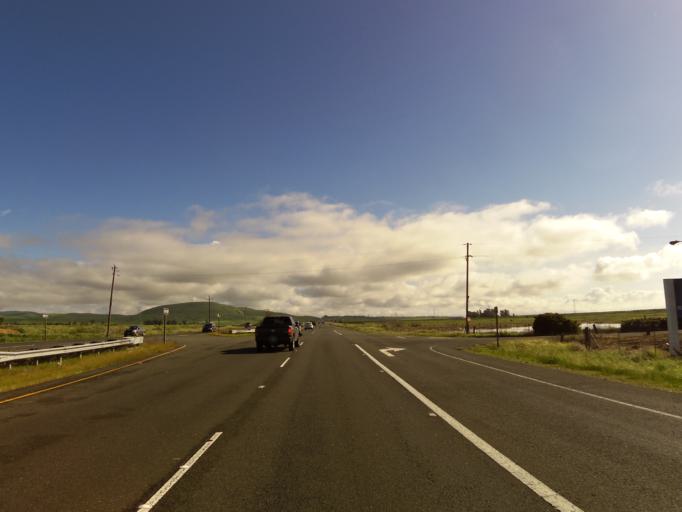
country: US
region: California
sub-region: Marin County
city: Black Point-Green Point
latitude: 38.1240
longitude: -122.4928
